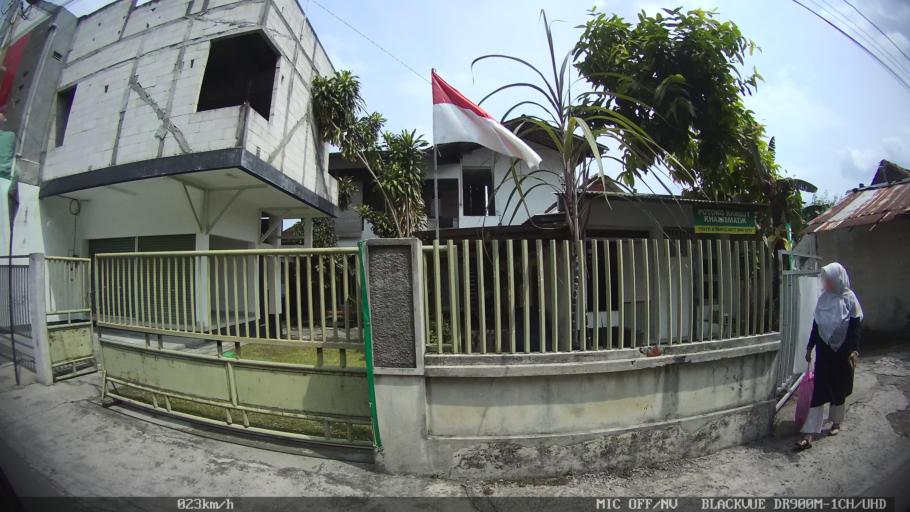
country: ID
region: Daerah Istimewa Yogyakarta
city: Yogyakarta
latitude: -7.7955
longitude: 110.3970
